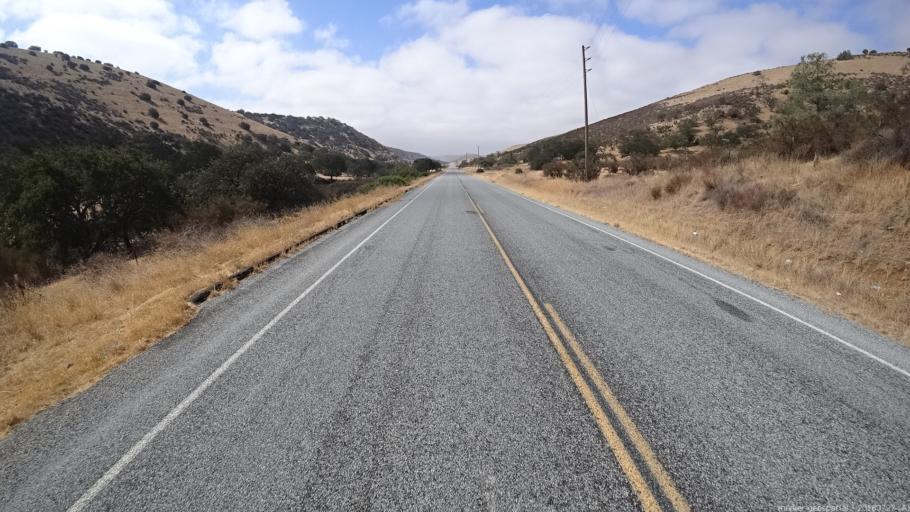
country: US
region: California
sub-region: Monterey County
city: King City
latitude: 36.2967
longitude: -121.0521
